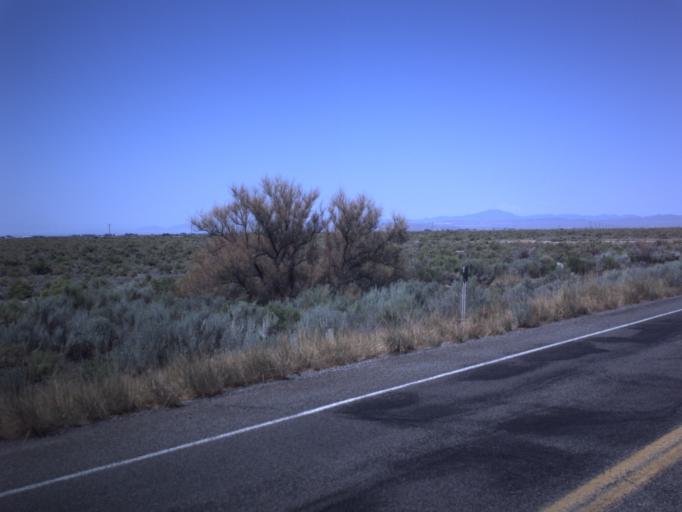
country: US
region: Utah
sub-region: Millard County
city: Delta
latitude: 39.4932
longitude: -112.5705
